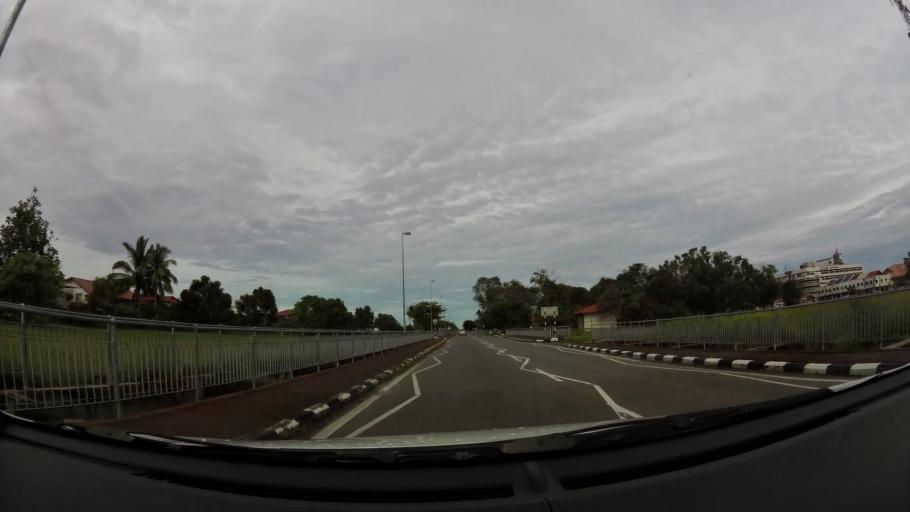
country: BN
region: Belait
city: Seria
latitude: 4.6127
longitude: 114.3329
